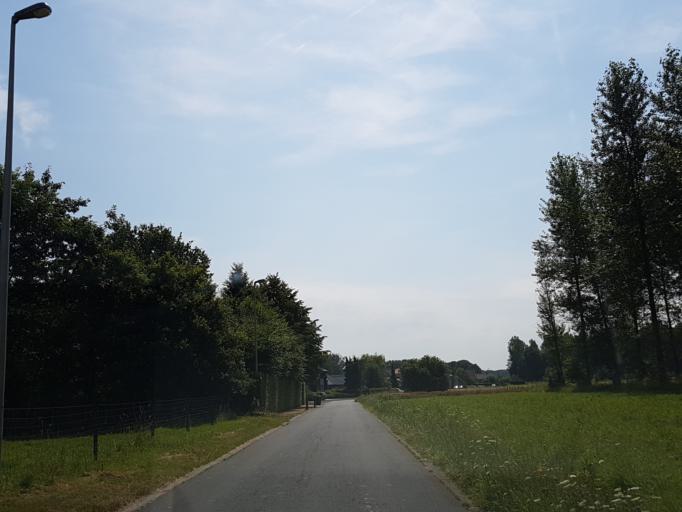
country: BE
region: Flanders
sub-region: Provincie Vlaams-Brabant
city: Steenokkerzeel
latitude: 50.9526
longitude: 4.5082
